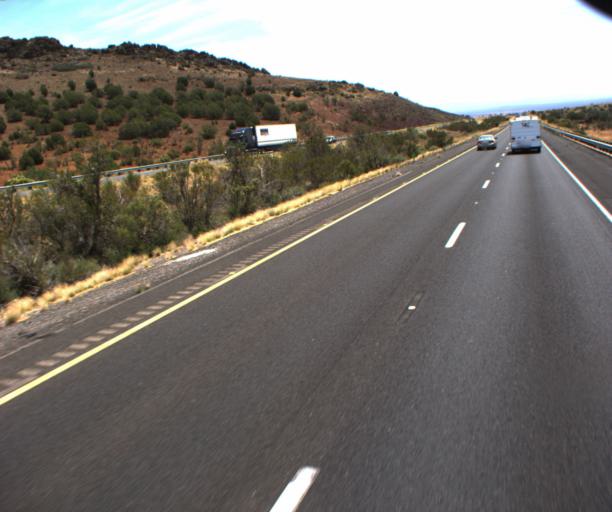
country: US
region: Arizona
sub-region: Yavapai County
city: Paulden
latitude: 35.2467
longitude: -112.6818
